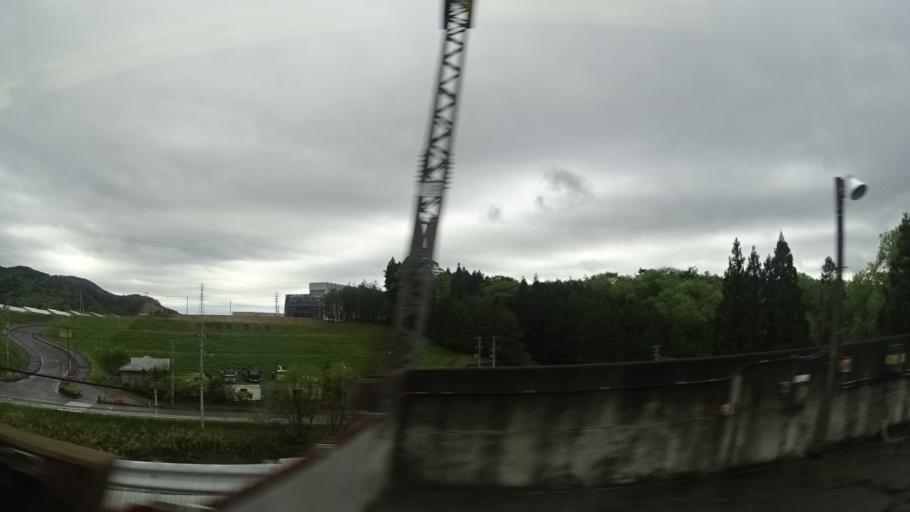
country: JP
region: Fukushima
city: Sukagawa
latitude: 37.1536
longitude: 140.2174
